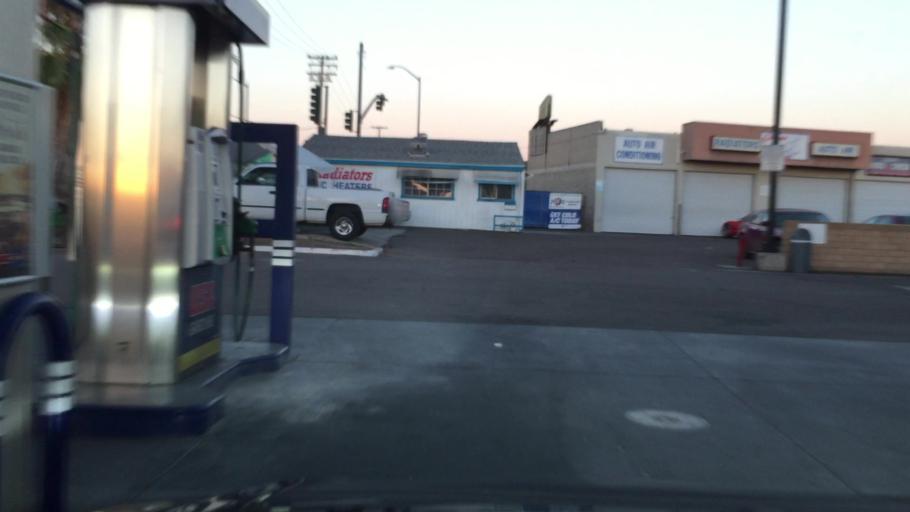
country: US
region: California
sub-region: San Diego County
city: Santee
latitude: 32.8189
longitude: -116.9620
